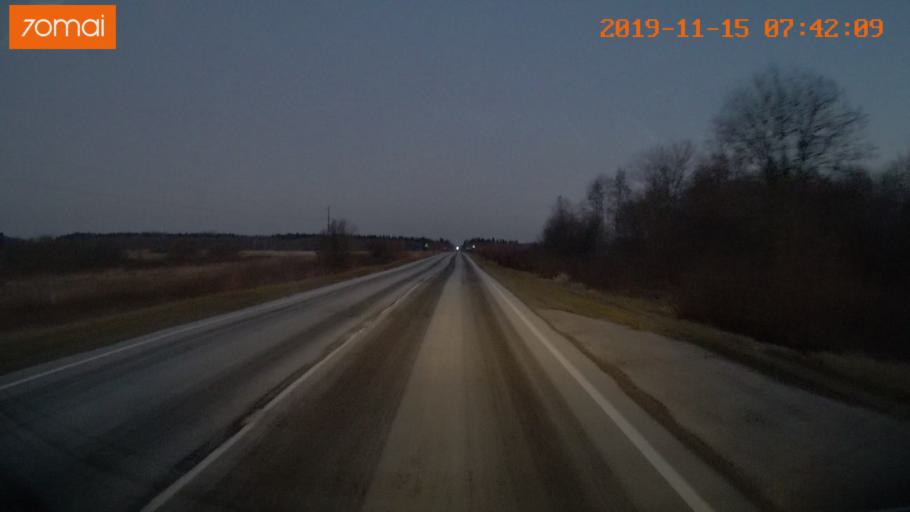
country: RU
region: Vologda
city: Sheksna
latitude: 58.7899
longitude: 38.3452
